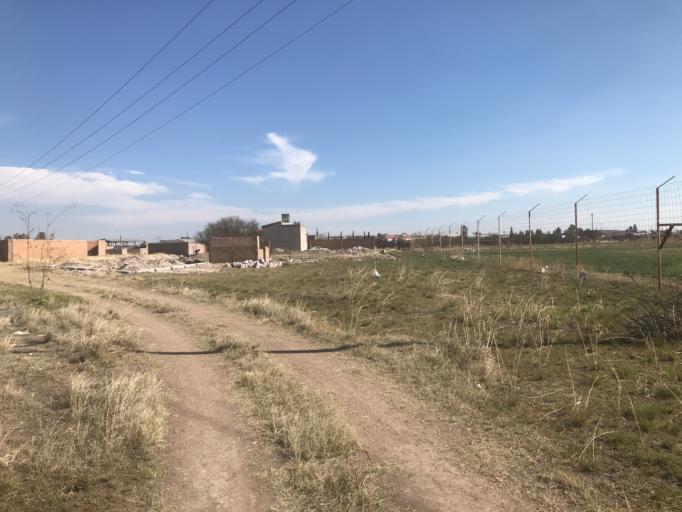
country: MX
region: Durango
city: Victoria de Durango
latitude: 24.0235
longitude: -104.5880
